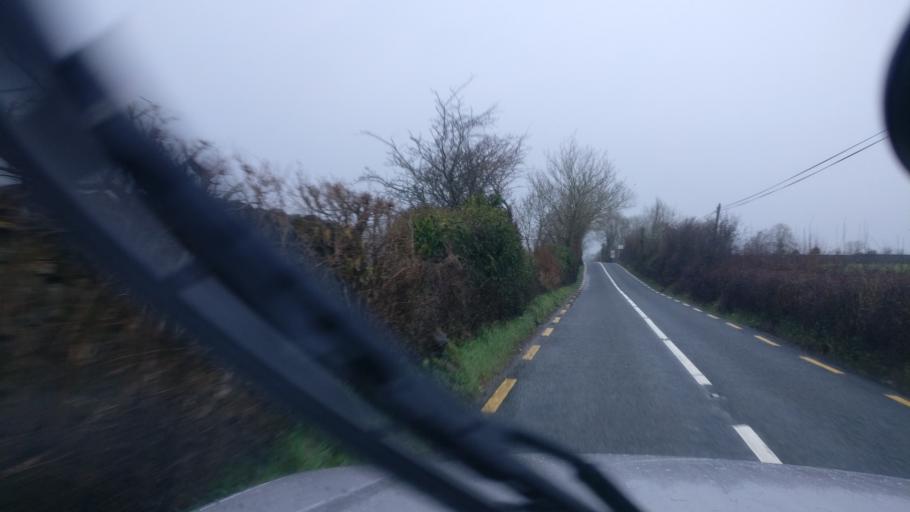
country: IE
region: Connaught
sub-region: County Galway
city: Loughrea
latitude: 53.1567
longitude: -8.4822
